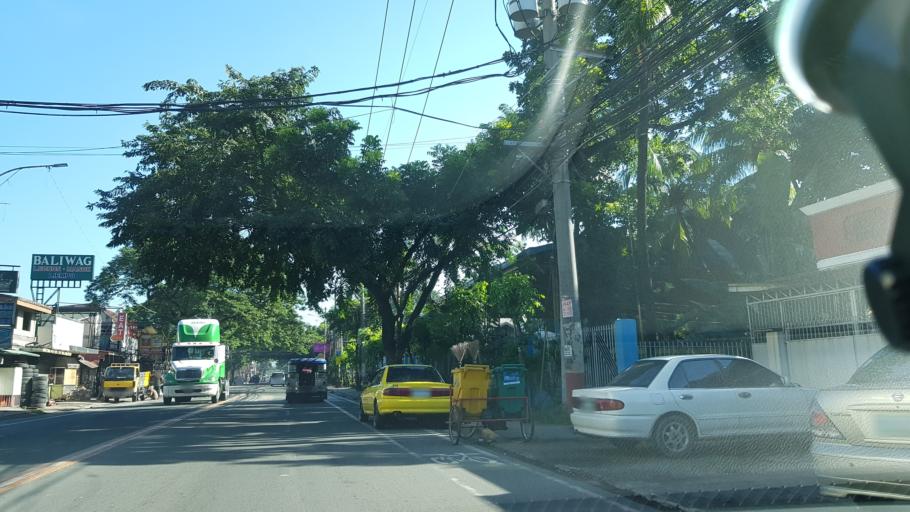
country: PH
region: Metro Manila
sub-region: Pasig
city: Pasig City
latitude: 14.5827
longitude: 121.0876
